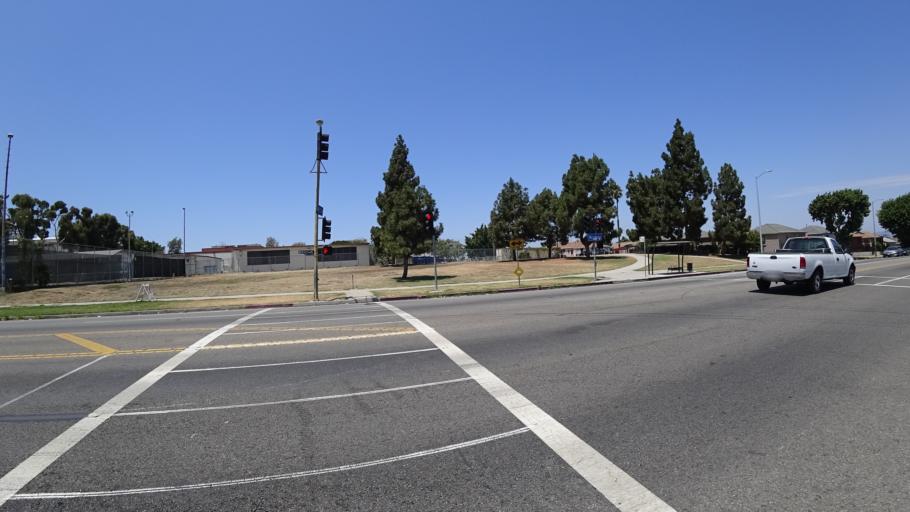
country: US
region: California
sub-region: Los Angeles County
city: Westmont
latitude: 33.9485
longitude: -118.3089
